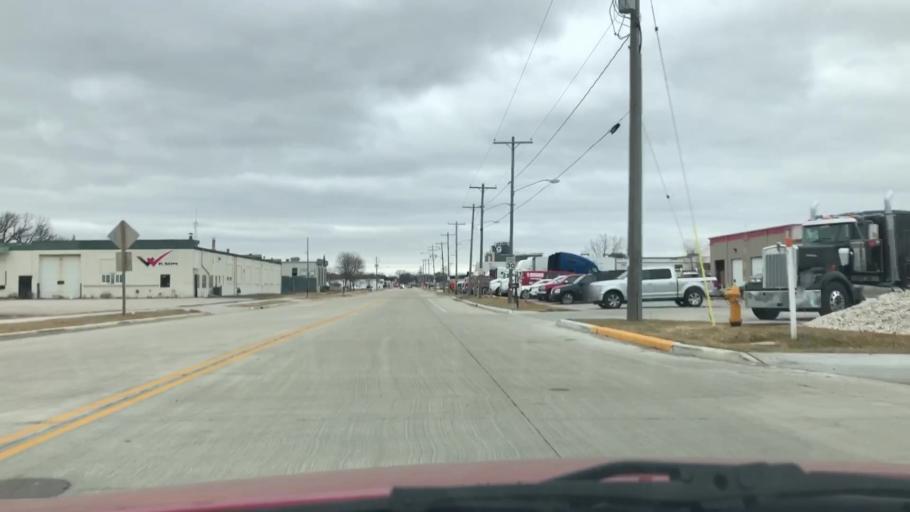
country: US
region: Wisconsin
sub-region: Brown County
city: Ashwaubenon
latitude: 44.4931
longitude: -88.0465
